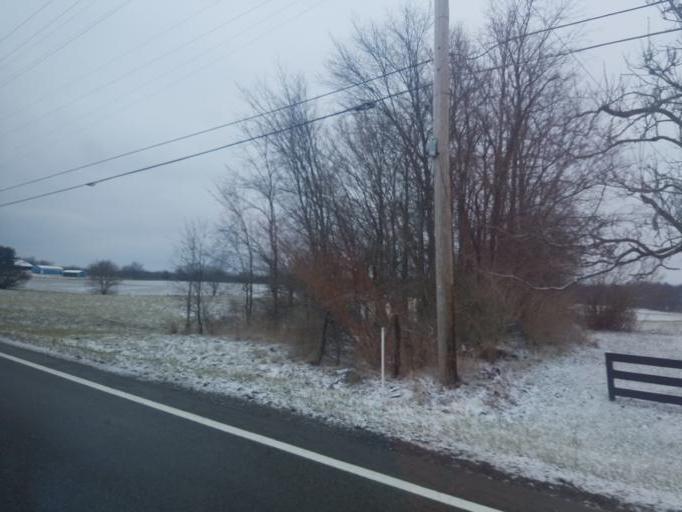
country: US
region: Ohio
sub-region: Licking County
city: Johnstown
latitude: 40.1693
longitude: -82.7093
